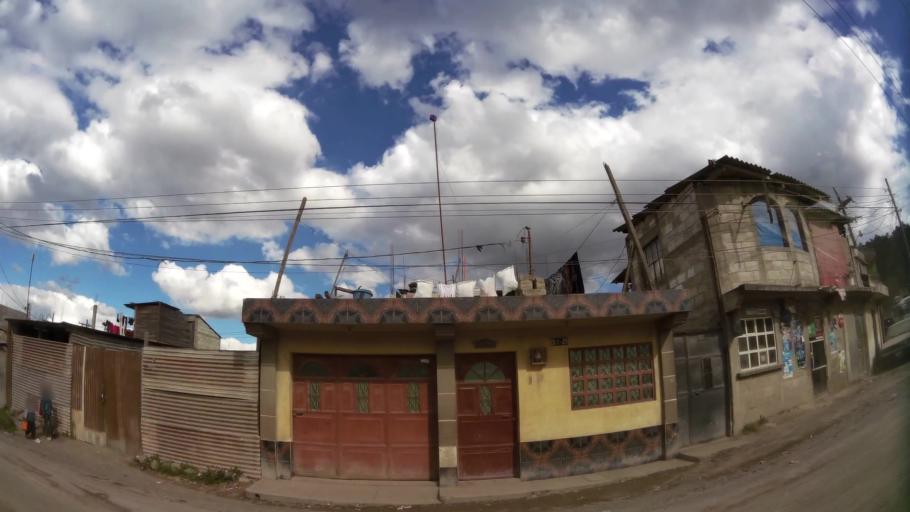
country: GT
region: Quetzaltenango
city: Quetzaltenango
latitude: 14.8282
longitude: -91.5369
